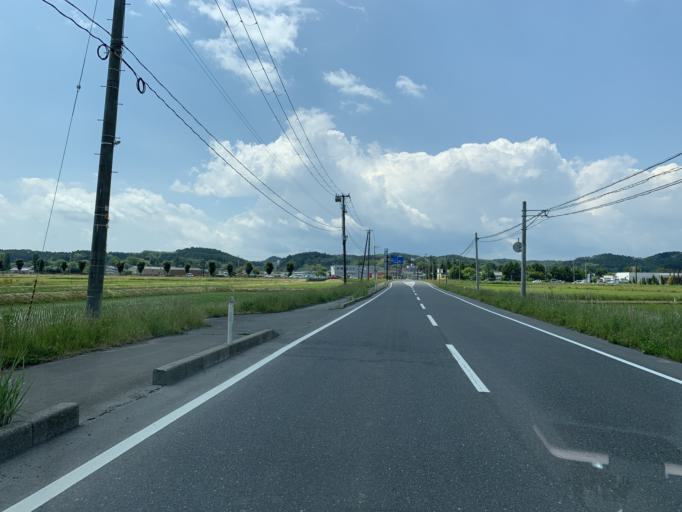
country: JP
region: Miyagi
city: Kogota
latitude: 38.5206
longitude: 141.0565
